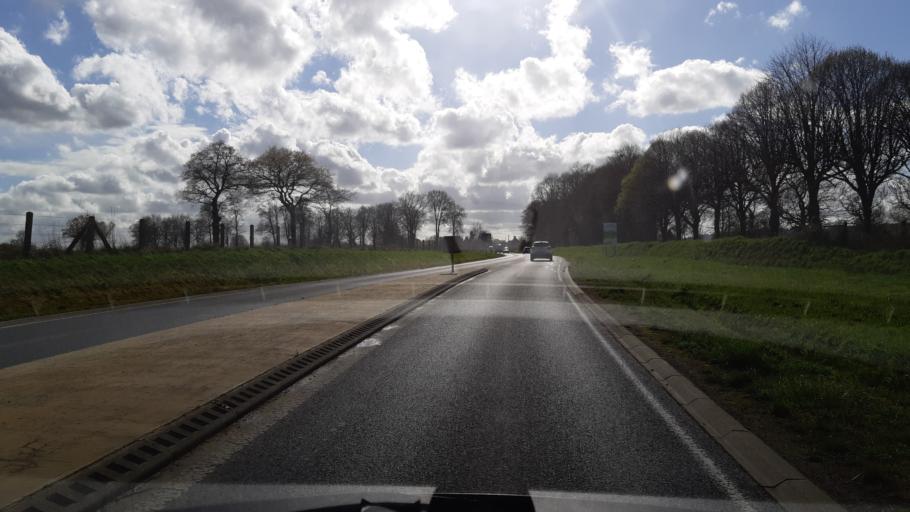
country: FR
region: Lower Normandy
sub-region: Departement de la Manche
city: Agneaux
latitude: 49.0312
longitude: -1.1369
